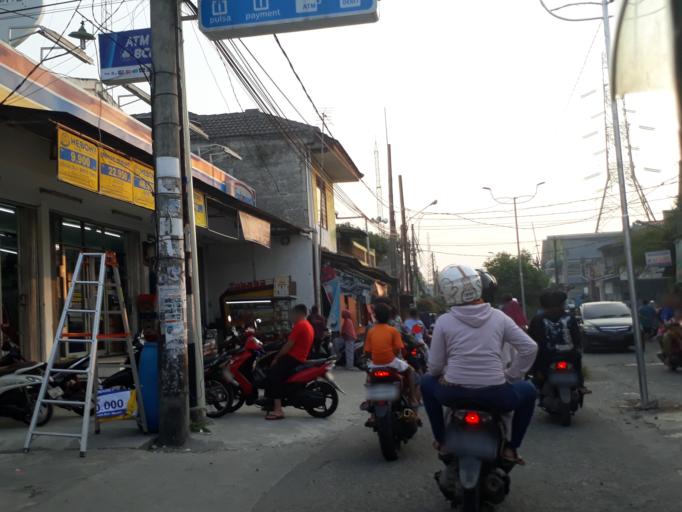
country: ID
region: West Java
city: Bekasi
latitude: -6.2433
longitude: 107.0500
